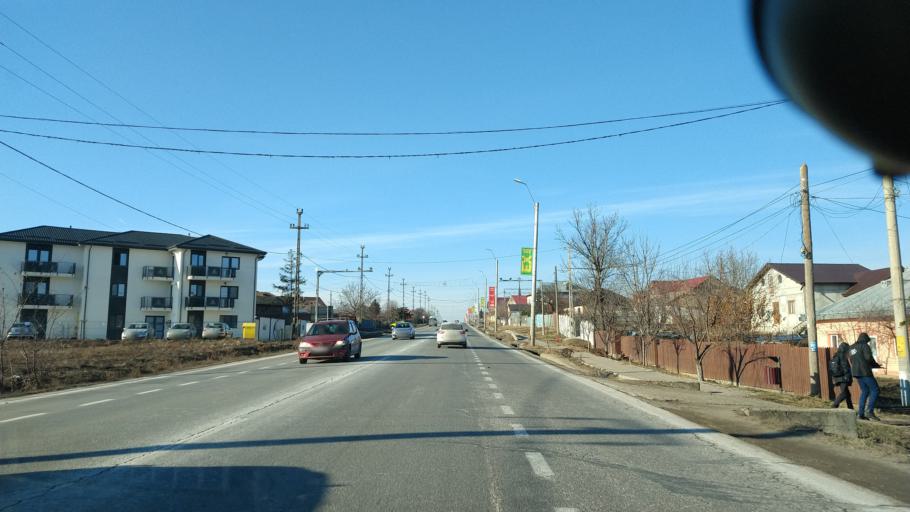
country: RO
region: Iasi
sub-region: Comuna Letcani
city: Letcani
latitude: 47.1911
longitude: 27.4275
